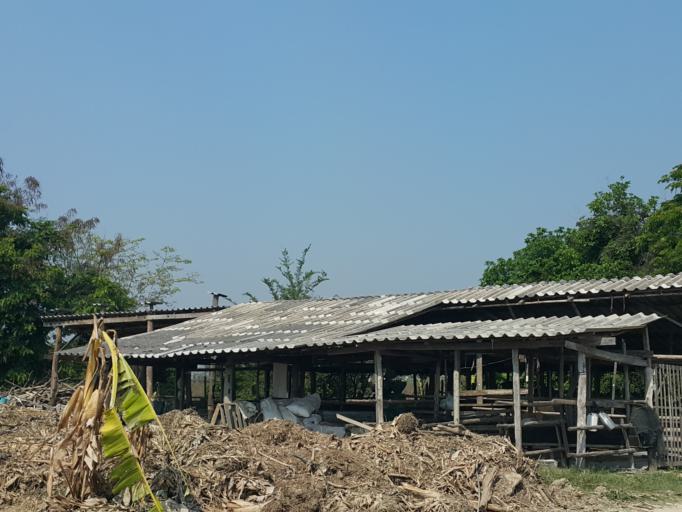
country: TH
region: Chiang Mai
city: San Kamphaeng
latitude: 18.7785
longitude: 99.0770
